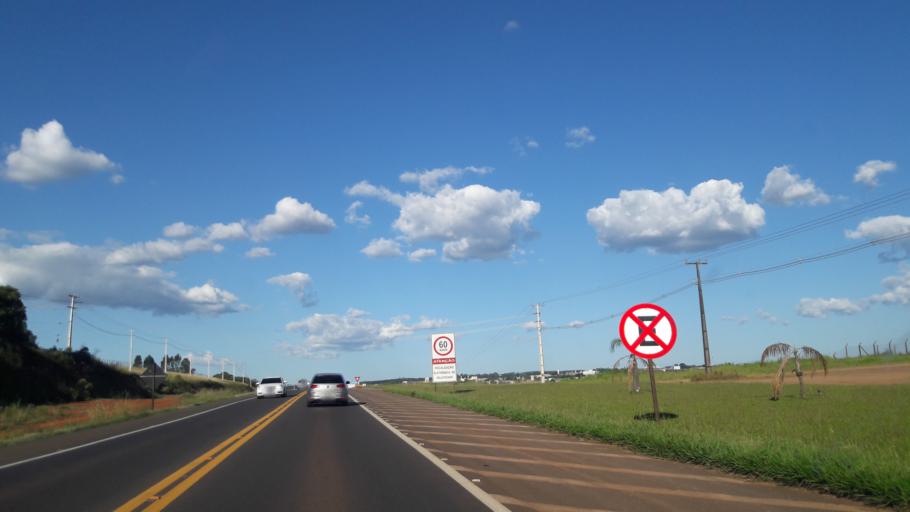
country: BR
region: Parana
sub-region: Guarapuava
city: Guarapuava
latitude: -25.3716
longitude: -51.4981
